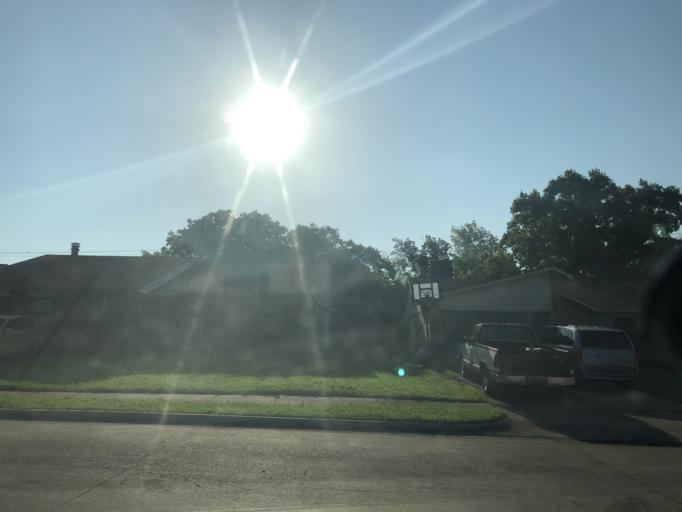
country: US
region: Texas
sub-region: Dallas County
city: Sunnyvale
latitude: 32.8166
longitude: -96.5980
